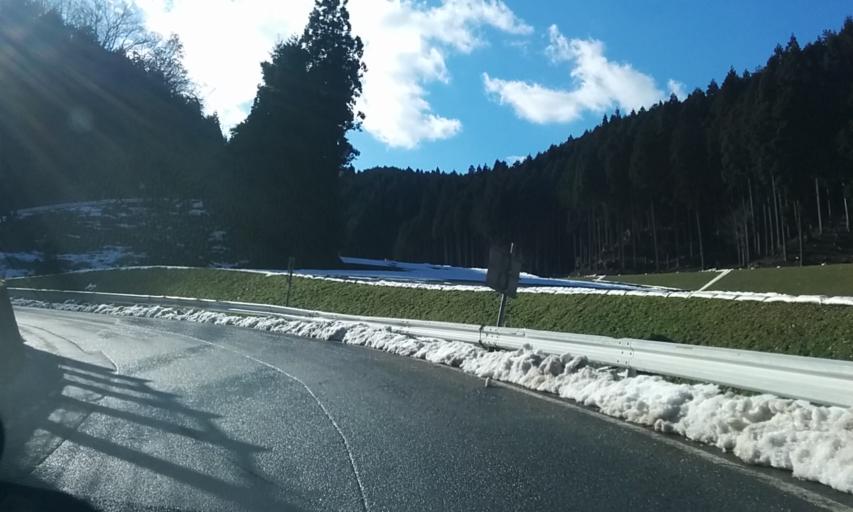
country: JP
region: Hyogo
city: Toyooka
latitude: 35.4129
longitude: 134.9565
